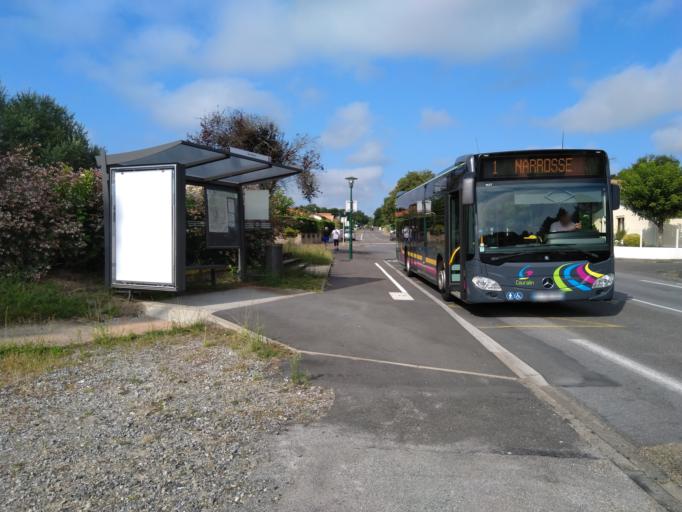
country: FR
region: Aquitaine
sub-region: Departement des Landes
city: Saint-Paul-les-Dax
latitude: 43.7337
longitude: -1.0778
